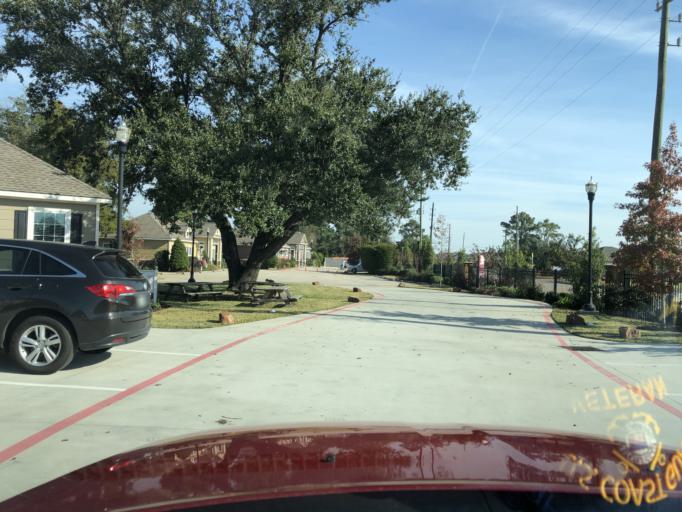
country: US
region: Texas
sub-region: Harris County
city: Tomball
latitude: 30.0352
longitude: -95.5579
